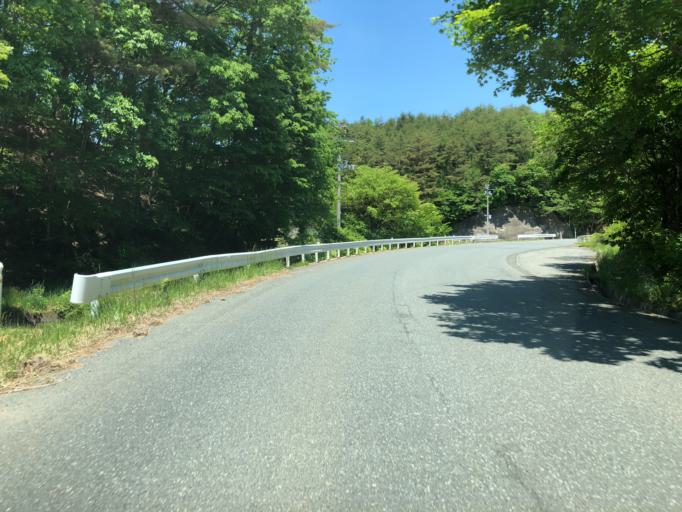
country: JP
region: Fukushima
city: Funehikimachi-funehiki
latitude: 37.5211
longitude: 140.7780
